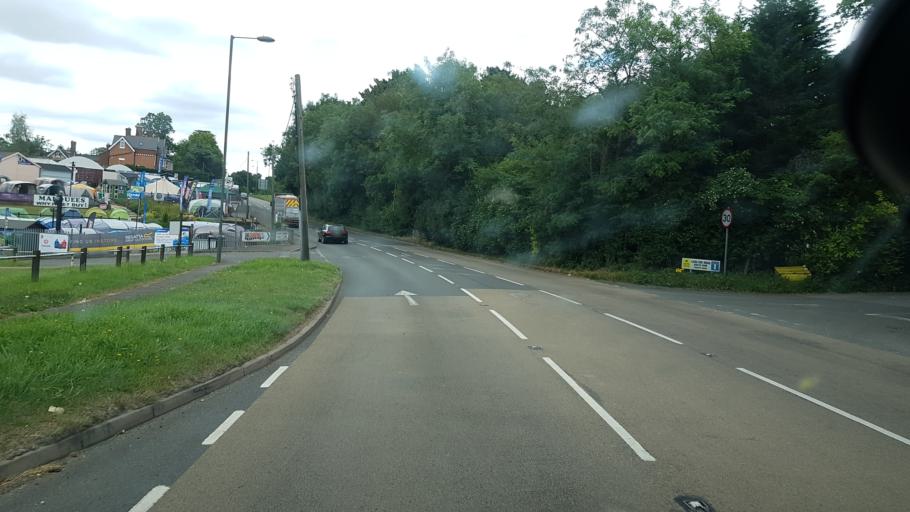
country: GB
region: England
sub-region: Surrey
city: Godstone
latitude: 51.2047
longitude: -0.0574
